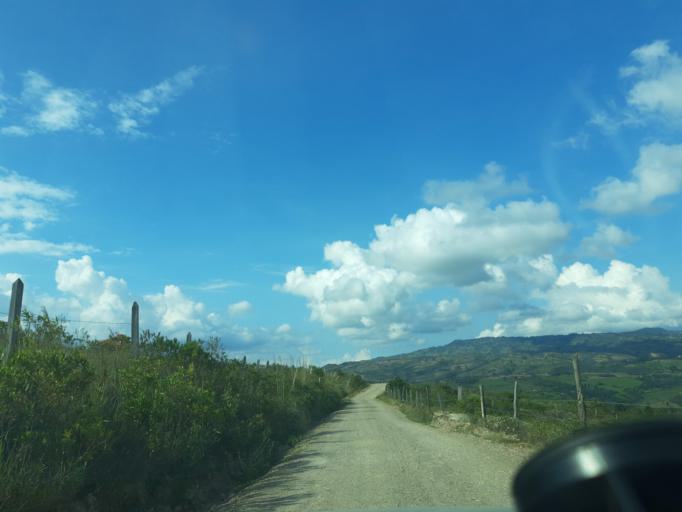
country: CO
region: Boyaca
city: Villa de Leiva
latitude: 5.6647
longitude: -73.5537
